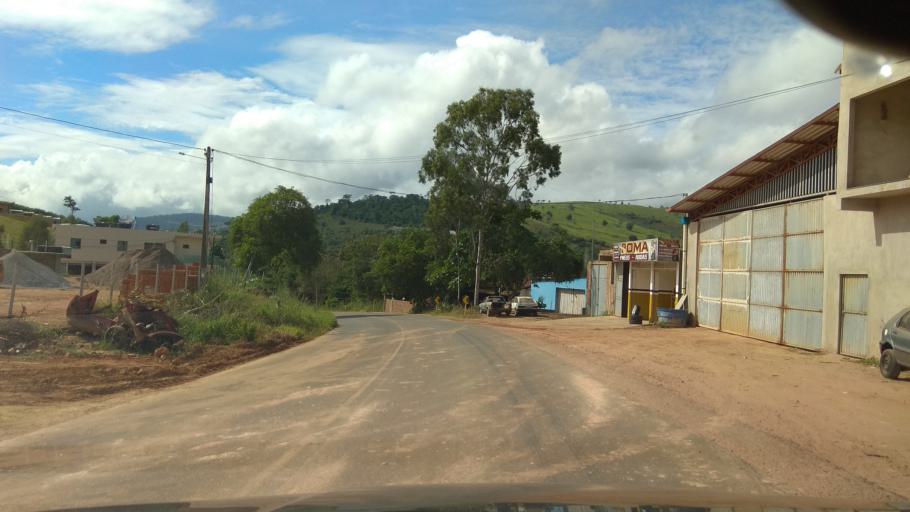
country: BR
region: Bahia
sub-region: Ubaira
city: Ubaira
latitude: -13.2710
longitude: -39.6572
